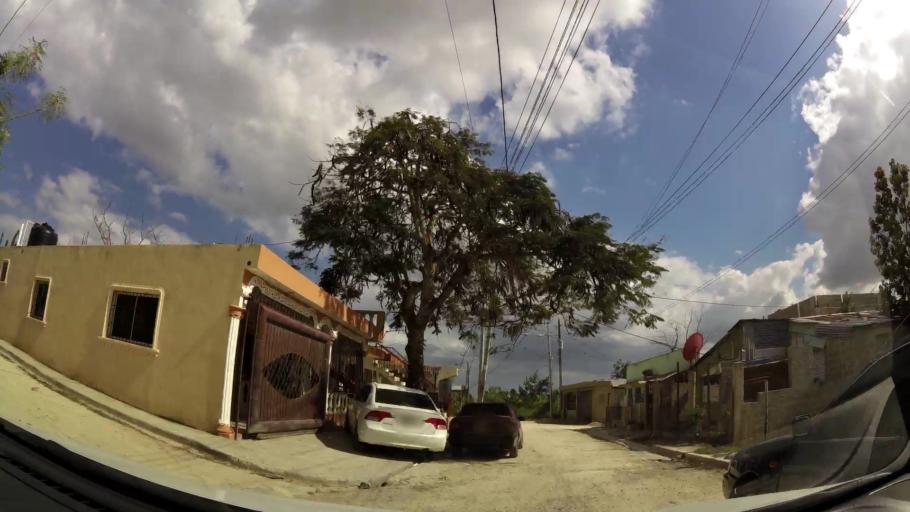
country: DO
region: Nacional
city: Ensanche Luperon
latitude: 18.5292
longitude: -69.8915
